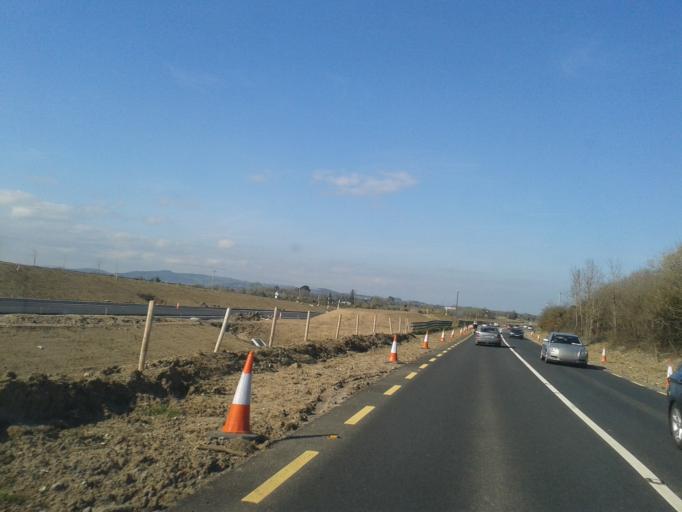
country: IE
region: Leinster
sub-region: Wicklow
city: Arklow
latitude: 52.8603
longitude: -6.1042
